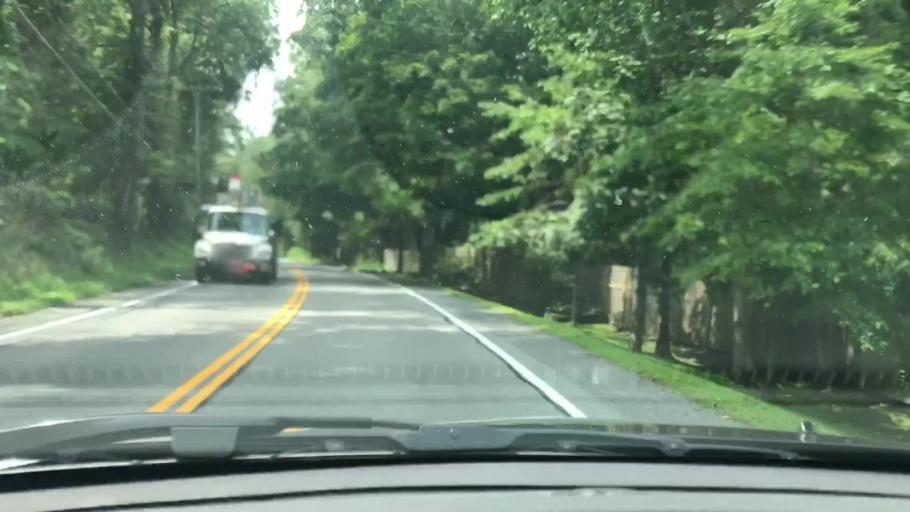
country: US
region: New York
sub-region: Westchester County
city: Bedford
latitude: 41.1976
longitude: -73.6669
